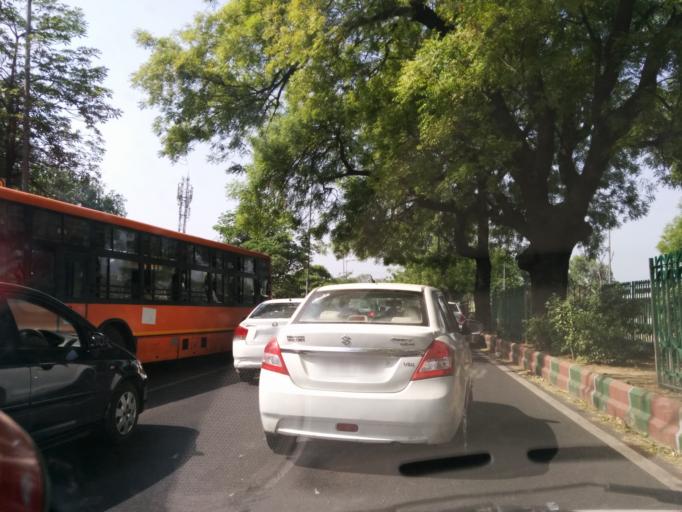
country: IN
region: NCT
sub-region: New Delhi
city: New Delhi
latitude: 28.5757
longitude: 77.2100
